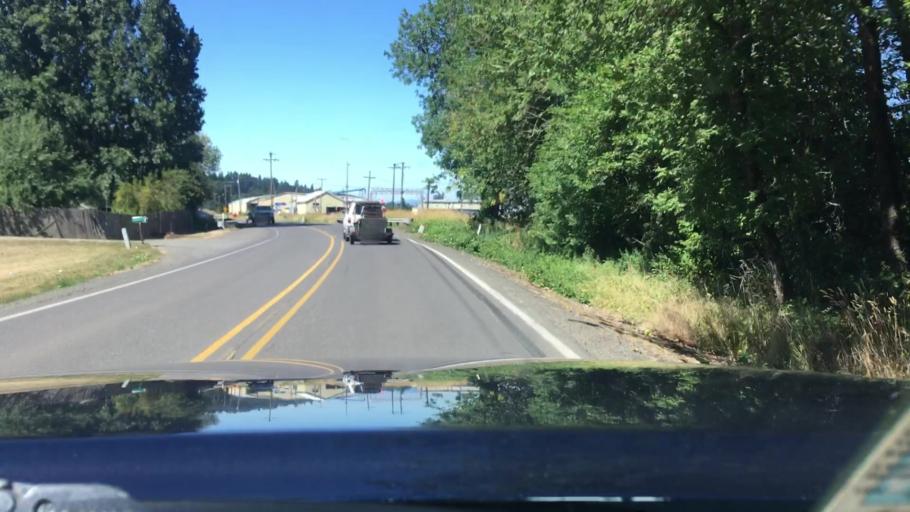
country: US
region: Oregon
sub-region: Lane County
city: Cottage Grove
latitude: 43.8310
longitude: -123.0450
